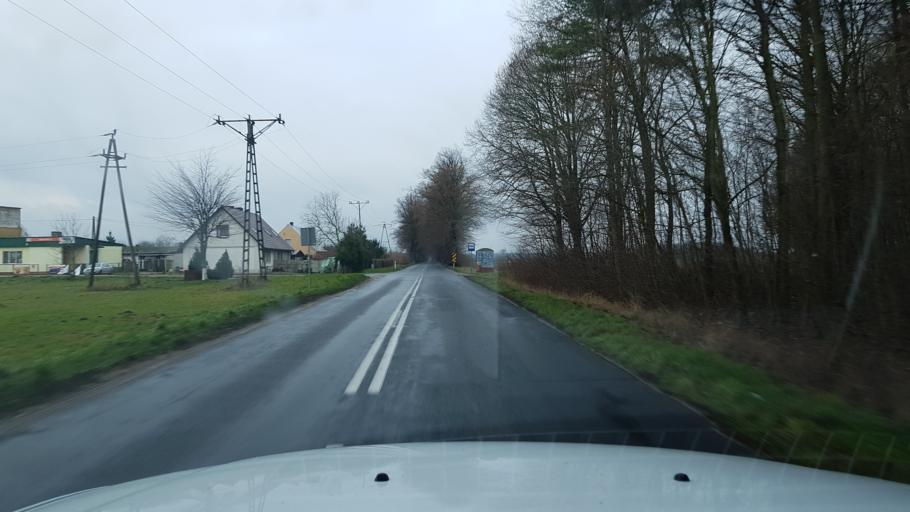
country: PL
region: West Pomeranian Voivodeship
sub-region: Powiat kolobrzeski
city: Grzybowo
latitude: 54.0717
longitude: 15.4272
